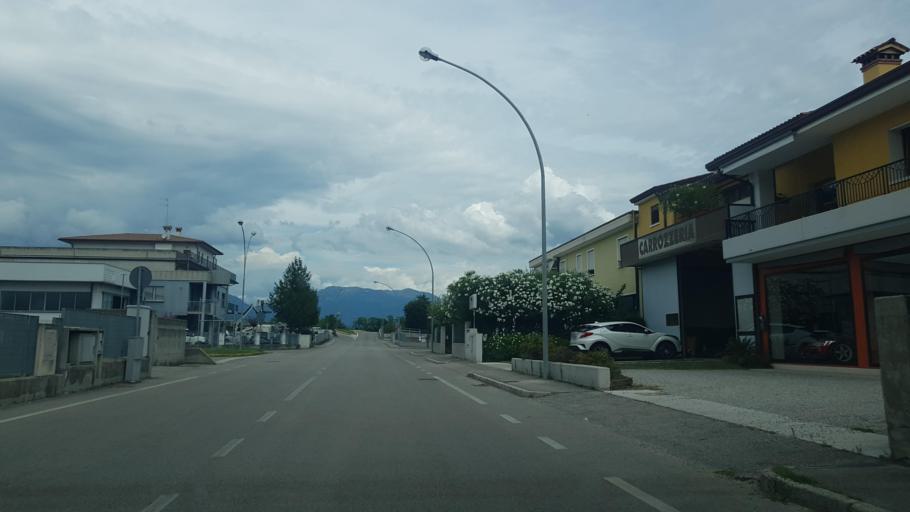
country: IT
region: Veneto
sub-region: Provincia di Treviso
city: Cornuda
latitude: 45.8368
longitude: 12.0140
